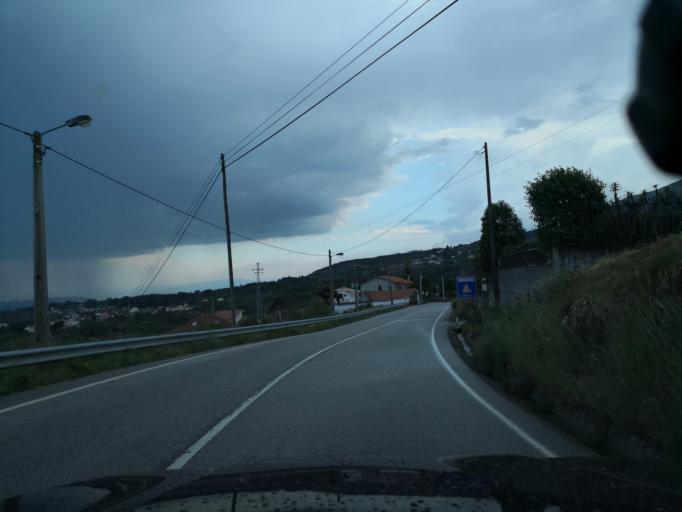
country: PT
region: Vila Real
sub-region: Vila Real
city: Vila Real
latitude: 41.3719
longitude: -7.7172
